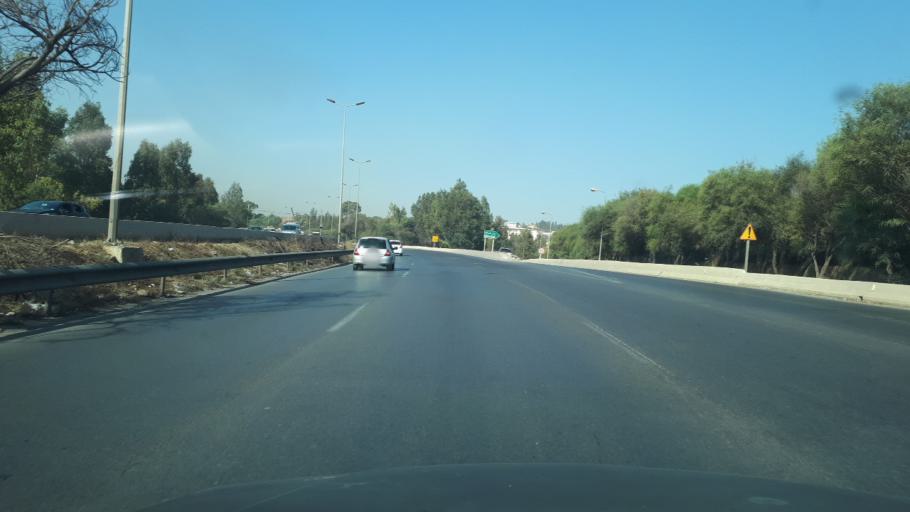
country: DZ
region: Tipaza
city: Baraki
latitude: 36.6787
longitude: 3.0615
